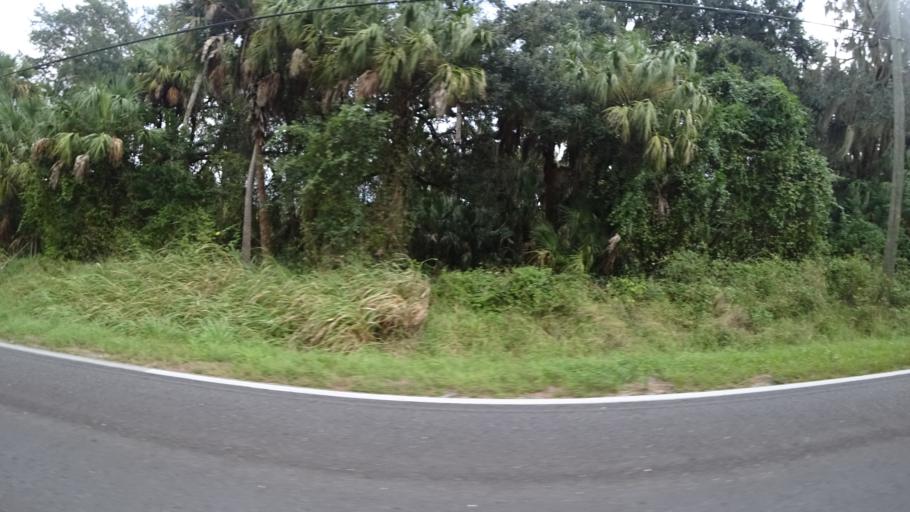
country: US
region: Florida
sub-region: Manatee County
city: Ellenton
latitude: 27.5644
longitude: -82.4789
